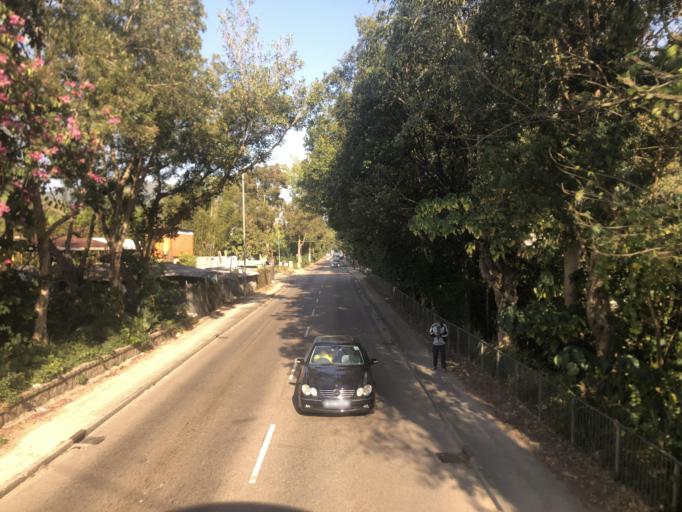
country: CN
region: Guangdong
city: Liantang
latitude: 22.5154
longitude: 114.1696
